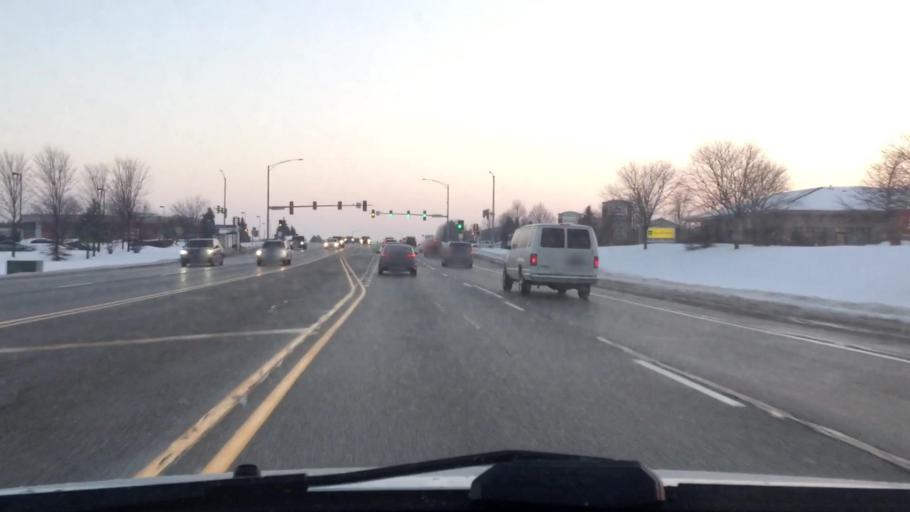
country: US
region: Illinois
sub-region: Kane County
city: Batavia
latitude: 41.8726
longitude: -88.3404
